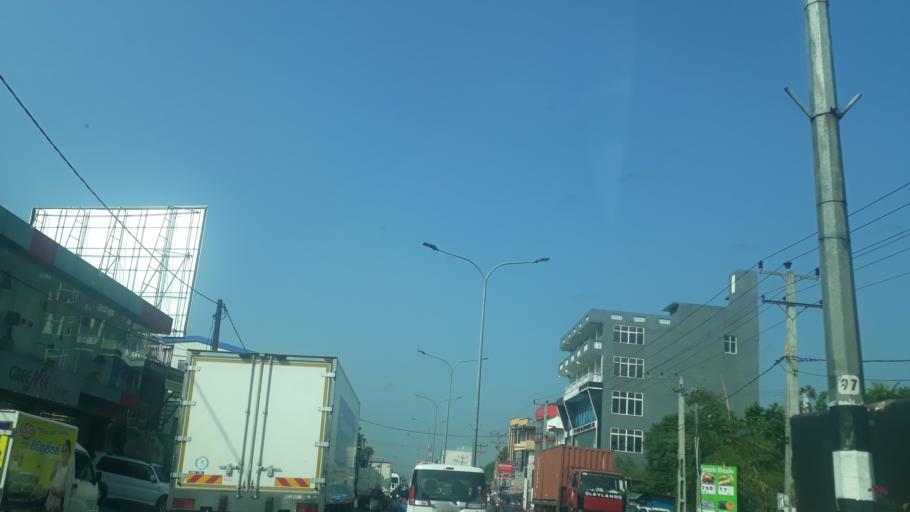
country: LK
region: Western
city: Kelaniya
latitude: 6.9689
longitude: 79.9116
